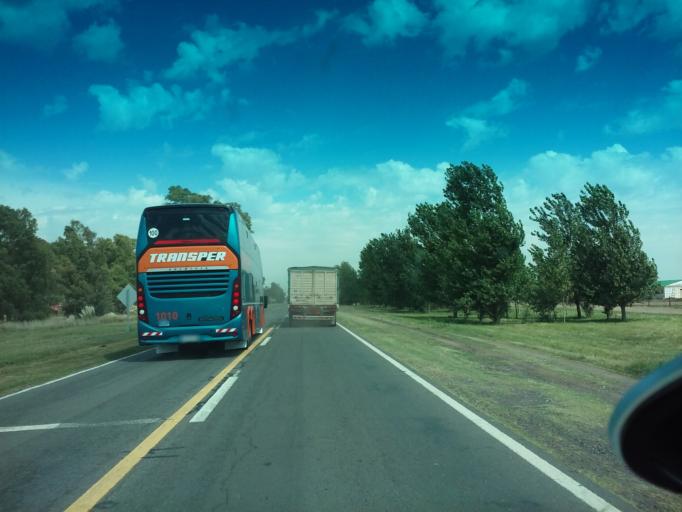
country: AR
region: Buenos Aires
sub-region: Partido de Carlos Casares
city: Carlos Casares
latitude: -35.6479
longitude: -61.3782
